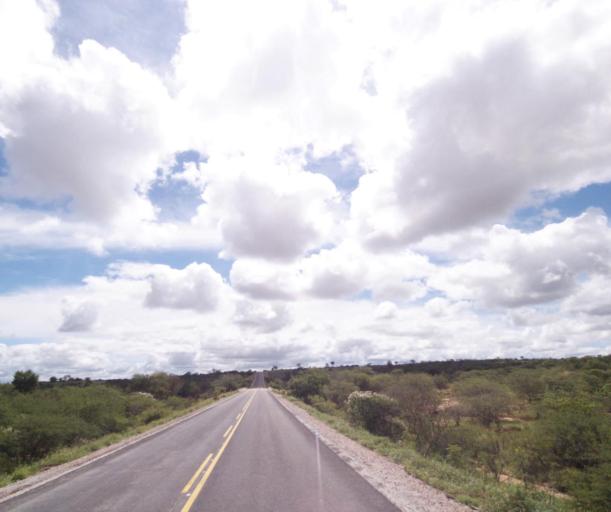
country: BR
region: Bahia
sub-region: Tanhacu
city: Tanhacu
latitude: -14.1564
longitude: -41.2655
